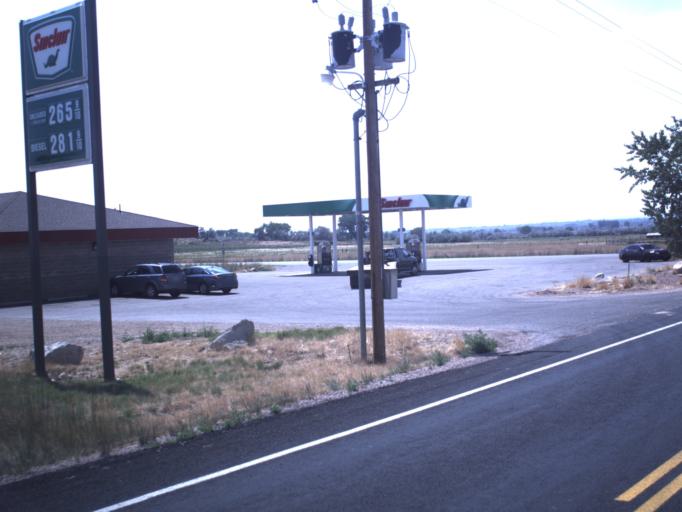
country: US
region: Utah
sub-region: Duchesne County
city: Roosevelt
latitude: 40.4037
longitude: -109.8206
